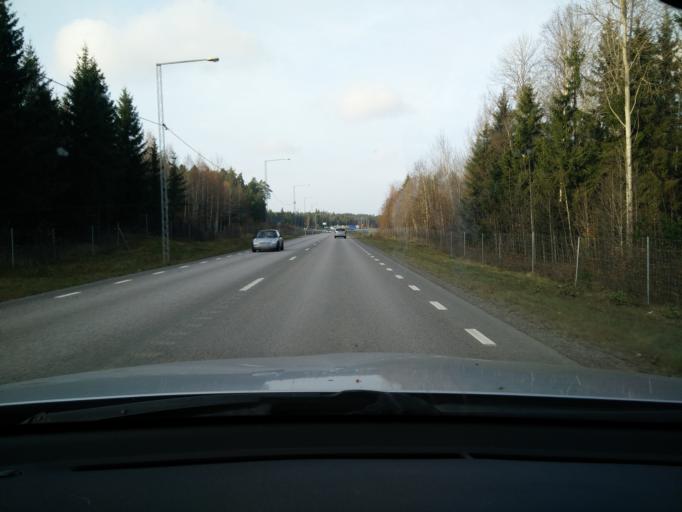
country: SE
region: Stockholm
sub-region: Taby Kommun
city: Taby
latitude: 59.4846
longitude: 18.1143
